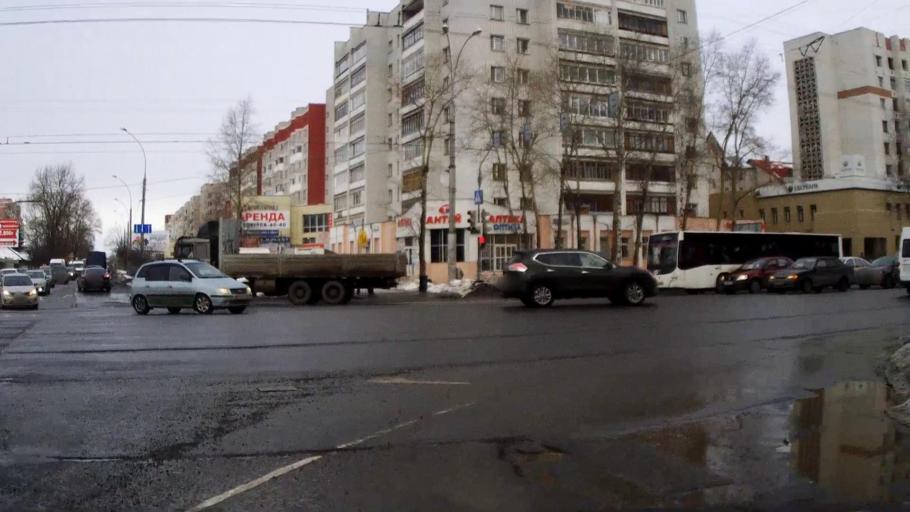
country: RU
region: Vologda
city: Vologda
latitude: 59.2128
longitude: 39.8514
